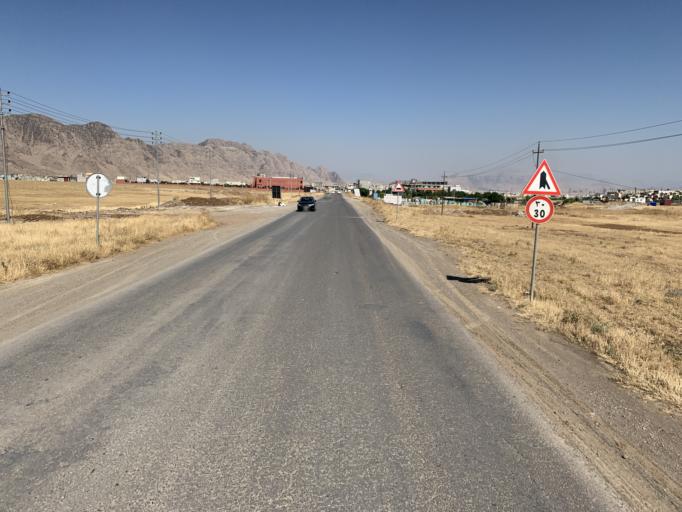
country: IQ
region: As Sulaymaniyah
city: Raniye
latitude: 36.2626
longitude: 44.8508
